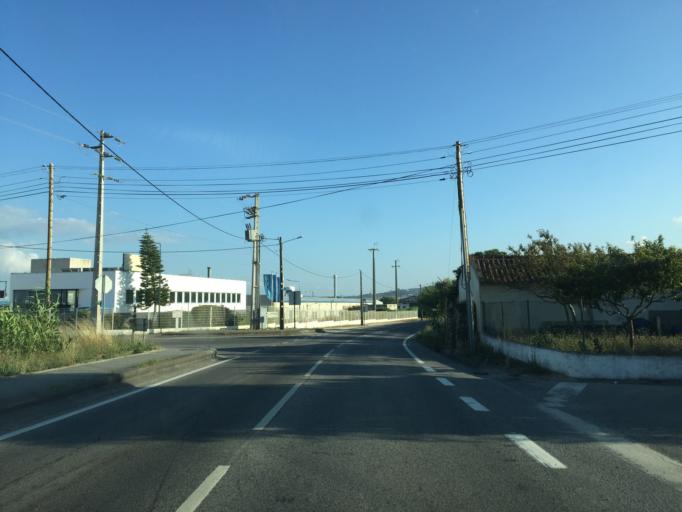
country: PT
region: Lisbon
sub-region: Alenquer
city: Alenquer
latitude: 39.0725
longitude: -8.9934
